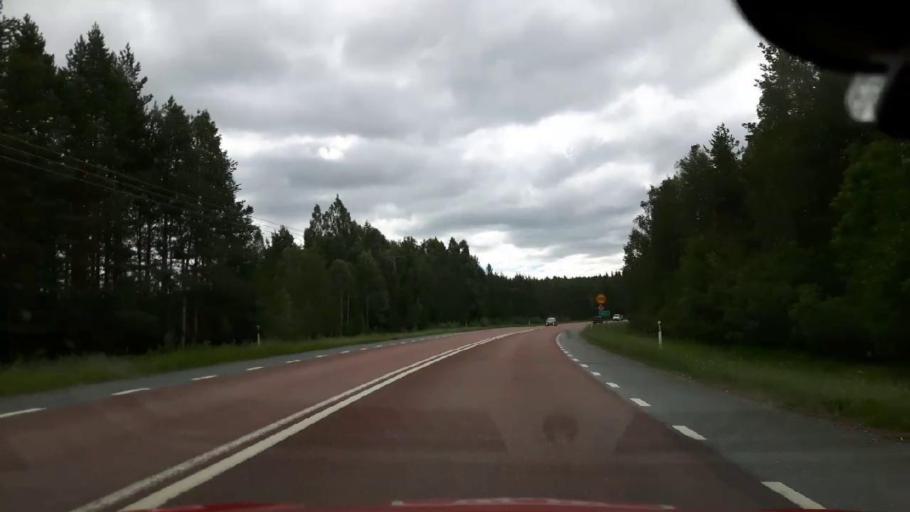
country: SE
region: Jaemtland
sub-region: Braecke Kommun
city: Braecke
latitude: 62.8129
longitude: 15.3611
